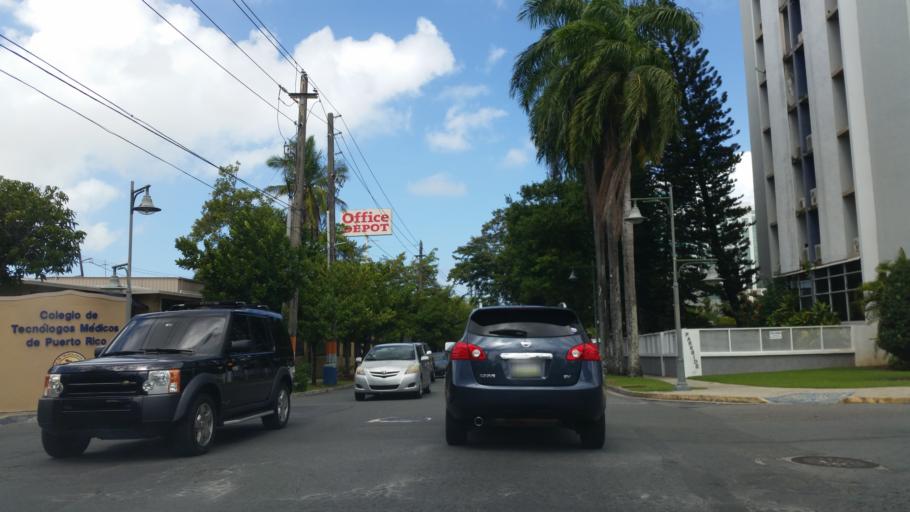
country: PR
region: Catano
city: Catano
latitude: 18.4075
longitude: -66.1028
